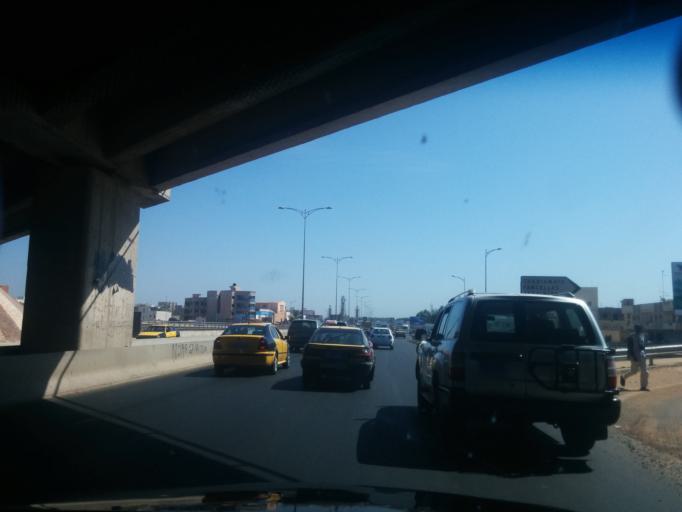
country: SN
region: Dakar
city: Grand Dakar
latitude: 14.7438
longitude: -17.4477
